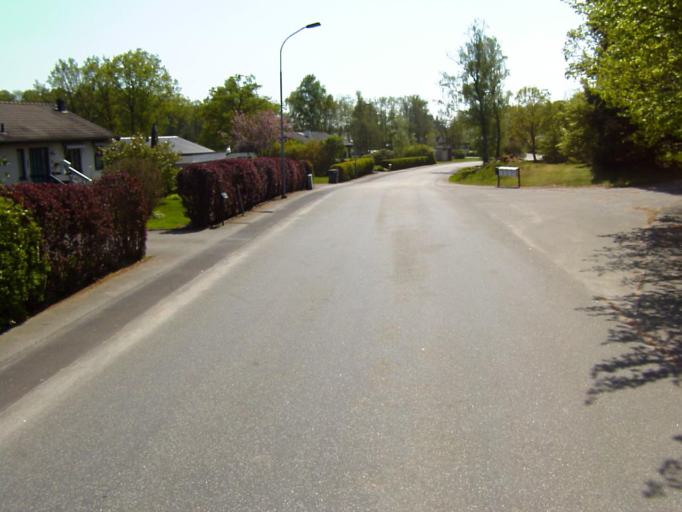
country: SE
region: Skane
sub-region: Kristianstads Kommun
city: Tollarp
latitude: 56.1704
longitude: 14.2900
